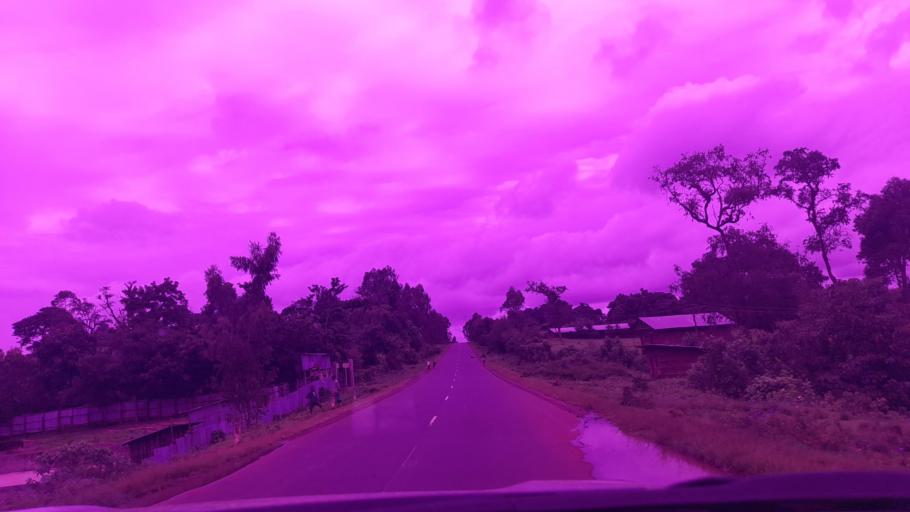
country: ET
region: Southern Nations, Nationalities, and People's Region
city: Bonga
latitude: 7.3042
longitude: 35.9950
